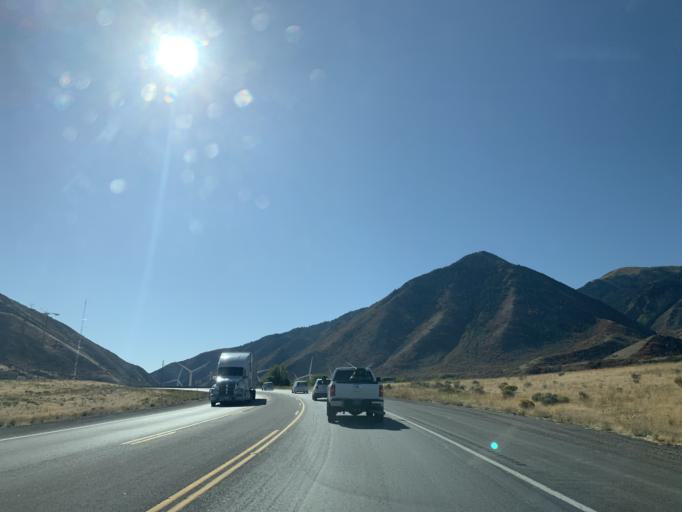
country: US
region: Utah
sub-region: Utah County
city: Mapleton
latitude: 40.0850
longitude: -111.5942
